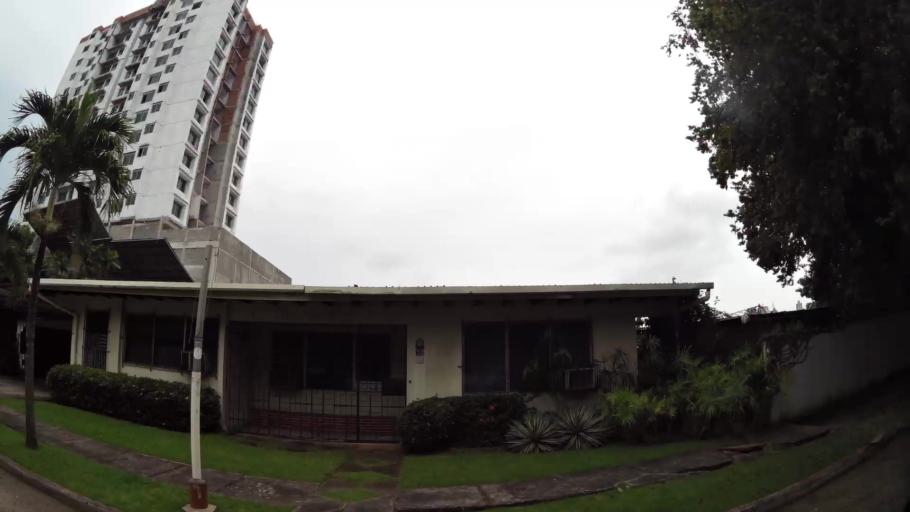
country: PA
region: Panama
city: Panama
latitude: 8.9984
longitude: -79.5293
